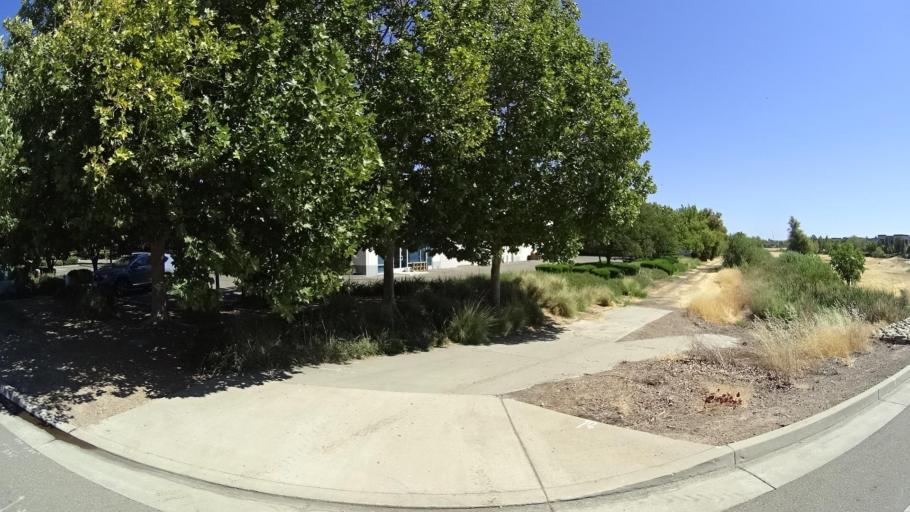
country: US
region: California
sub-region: Placer County
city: Roseville
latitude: 38.8122
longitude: -121.2962
